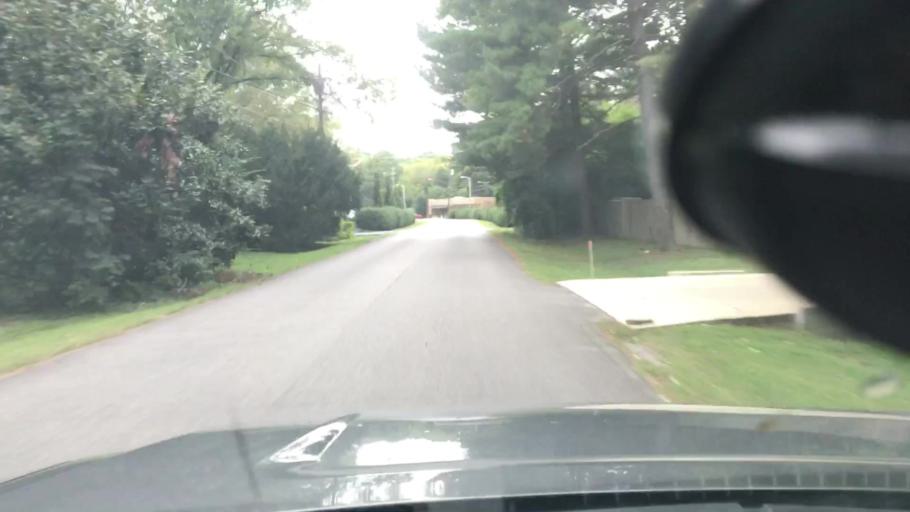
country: US
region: Tennessee
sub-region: Davidson County
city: Oak Hill
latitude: 36.1123
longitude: -86.7808
